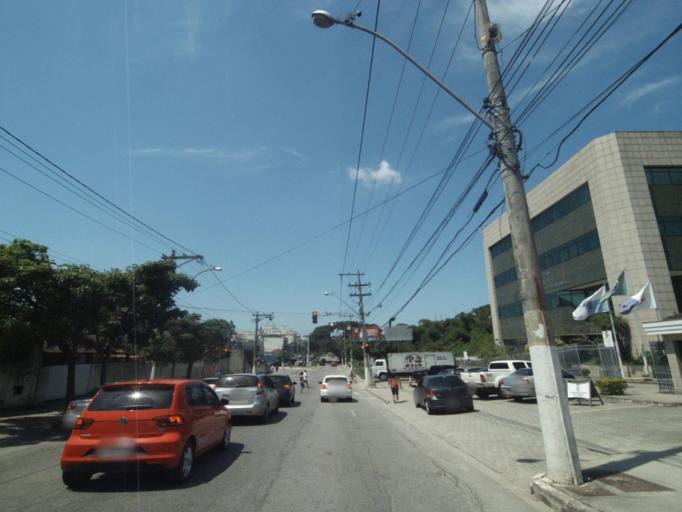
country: BR
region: Rio de Janeiro
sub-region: Niteroi
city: Niteroi
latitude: -22.9077
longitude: -43.0634
